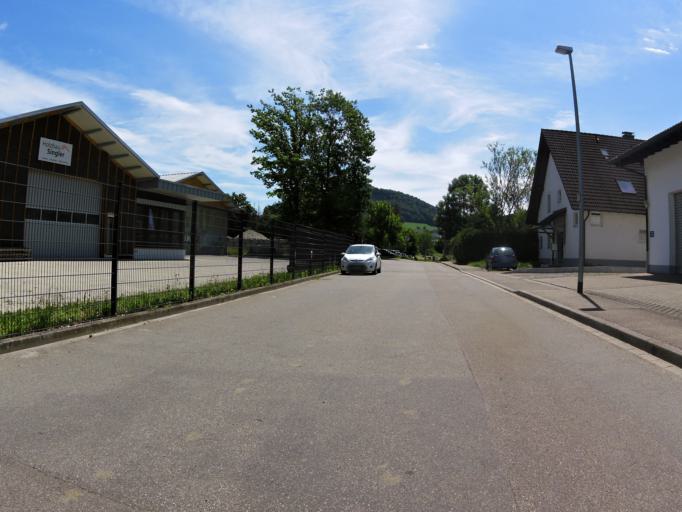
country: DE
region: Baden-Wuerttemberg
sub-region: Freiburg Region
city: Seelbach
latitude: 48.3245
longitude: 7.9313
